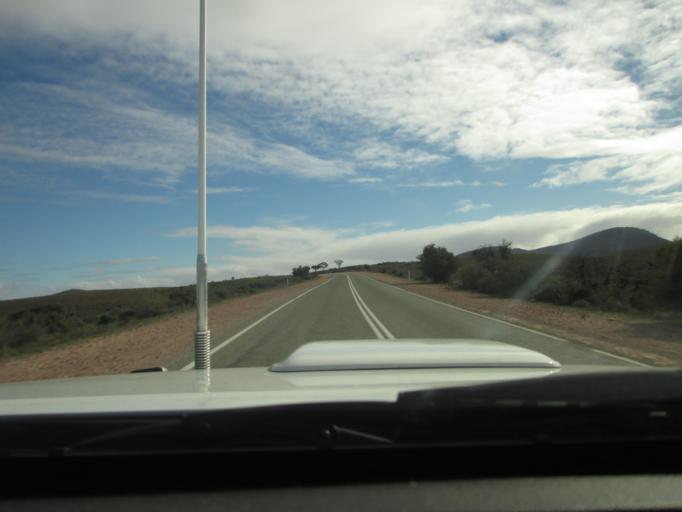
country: AU
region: South Australia
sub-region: Flinders Ranges
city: Quorn
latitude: -31.8114
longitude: 138.3686
